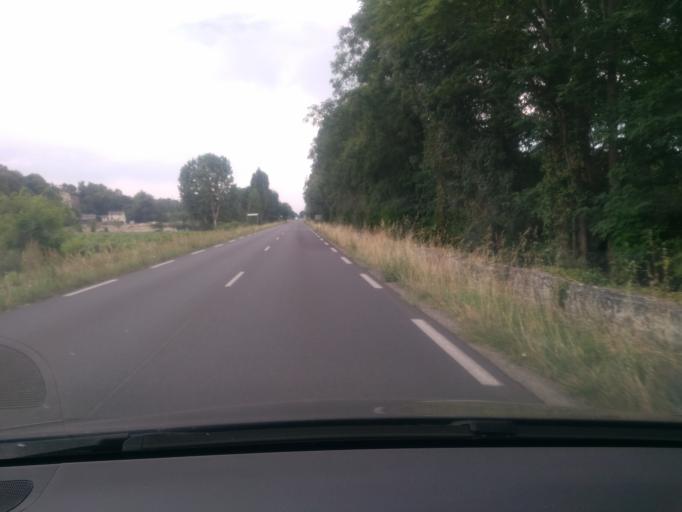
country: FR
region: Pays de la Loire
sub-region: Departement de Maine-et-Loire
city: Varennes-sur-Loire
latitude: 47.2222
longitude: 0.0396
